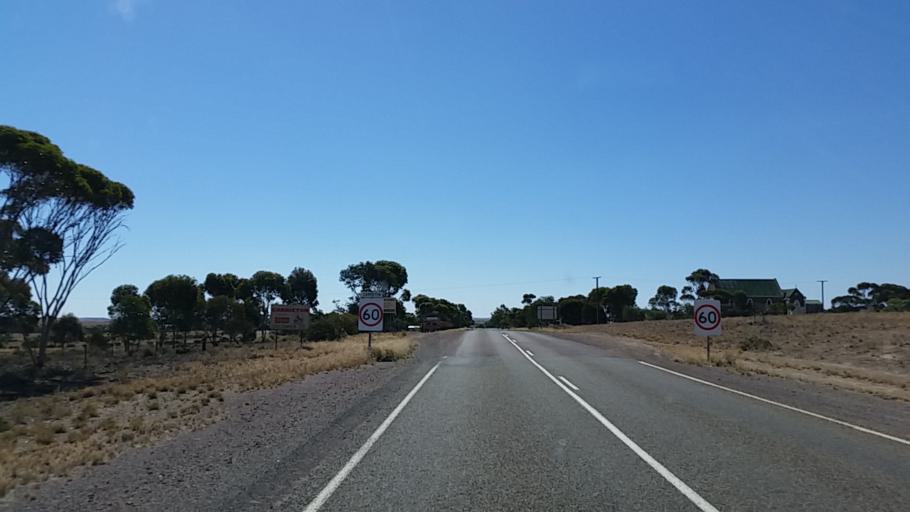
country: AU
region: South Australia
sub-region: Flinders Ranges
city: Quorn
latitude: -32.4288
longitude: 138.5313
